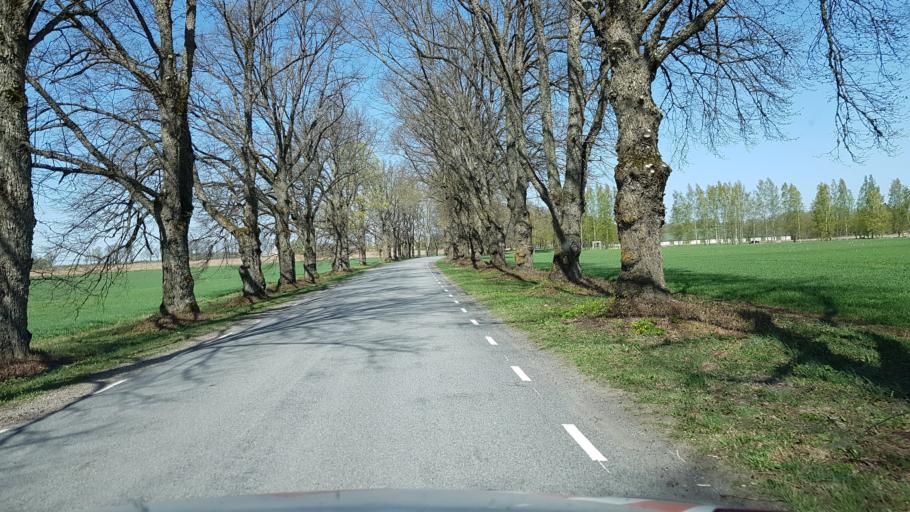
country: EE
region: Viljandimaa
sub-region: Vohma linn
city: Vohma
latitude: 58.5460
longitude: 25.5682
